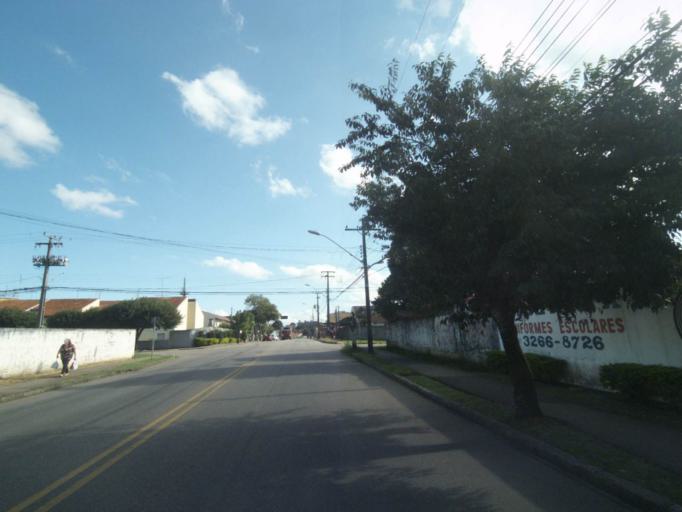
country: BR
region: Parana
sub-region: Pinhais
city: Pinhais
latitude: -25.4420
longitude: -49.2078
